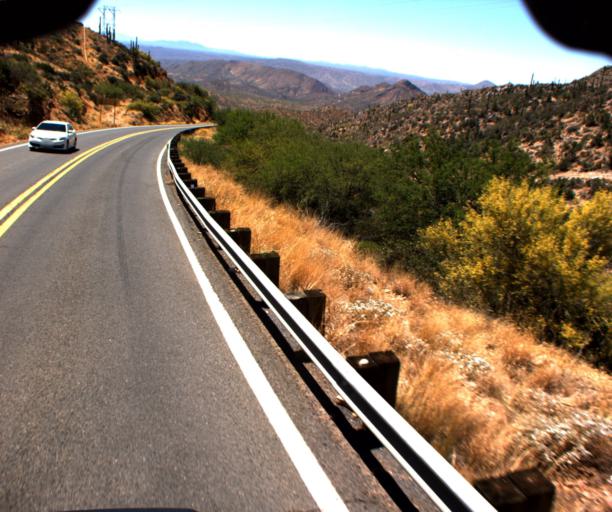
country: US
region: Arizona
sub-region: Pinal County
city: Superior
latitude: 33.1983
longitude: -111.0544
